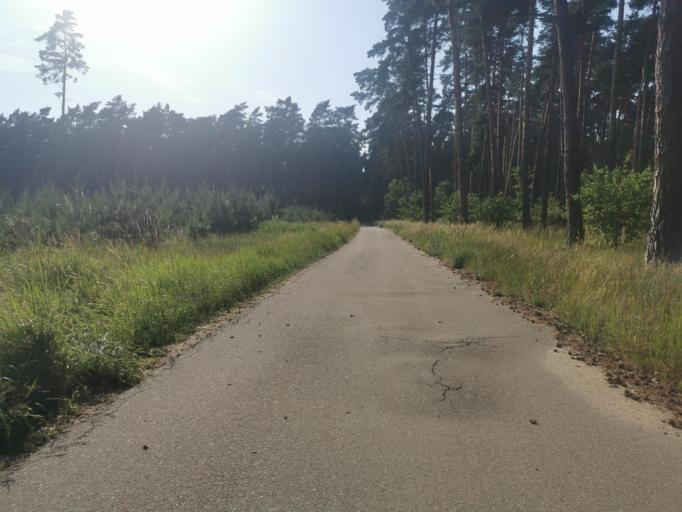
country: CZ
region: South Moravian
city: Ratiskovice
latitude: 48.9199
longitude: 17.2057
